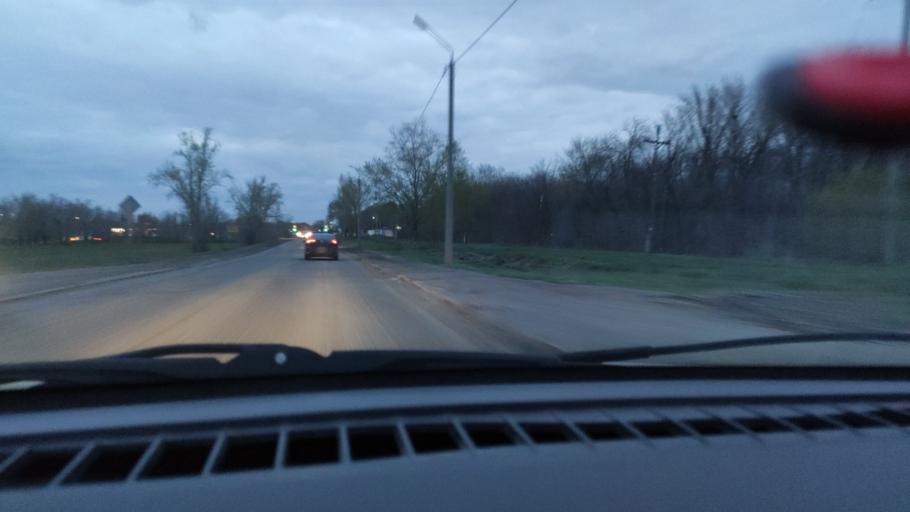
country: RU
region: Orenburg
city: Tatarskaya Kargala
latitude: 51.8640
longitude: 55.1382
